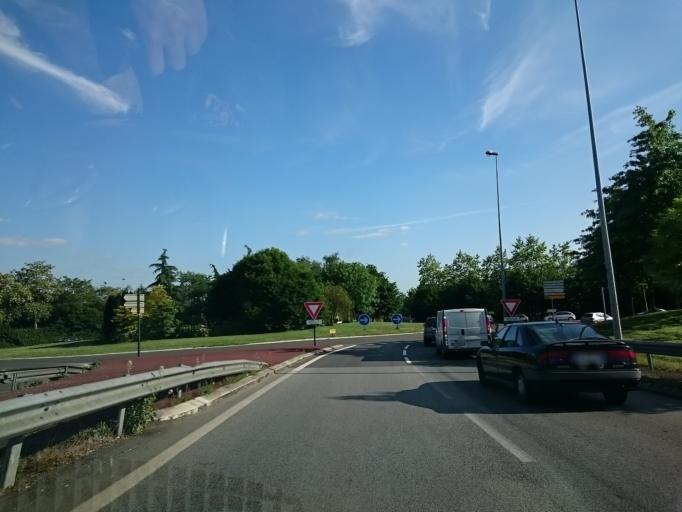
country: FR
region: Brittany
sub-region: Departement d'Ille-et-Vilaine
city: Vern-sur-Seiche
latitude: 48.0453
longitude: -1.6081
